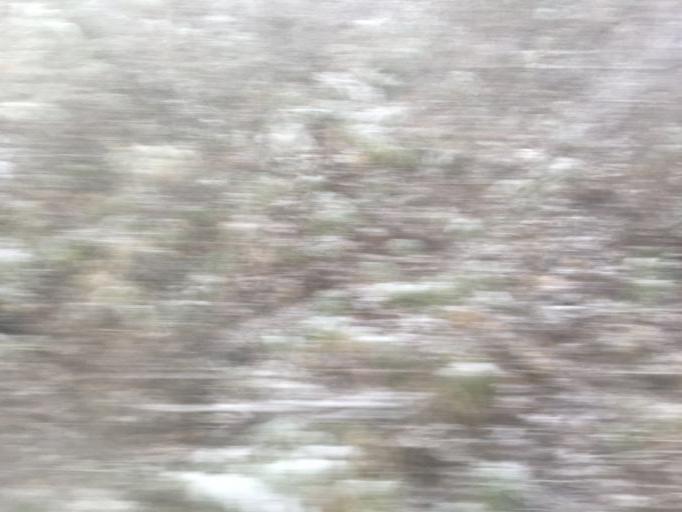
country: JP
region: Aomori
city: Goshogawara
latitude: 41.1021
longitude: 140.5281
